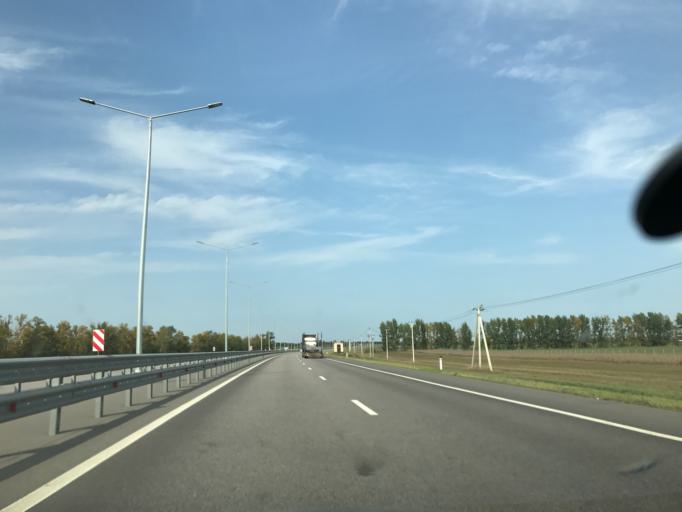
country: RU
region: Voronezj
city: Podkletnoye
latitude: 51.5117
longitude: 39.5134
